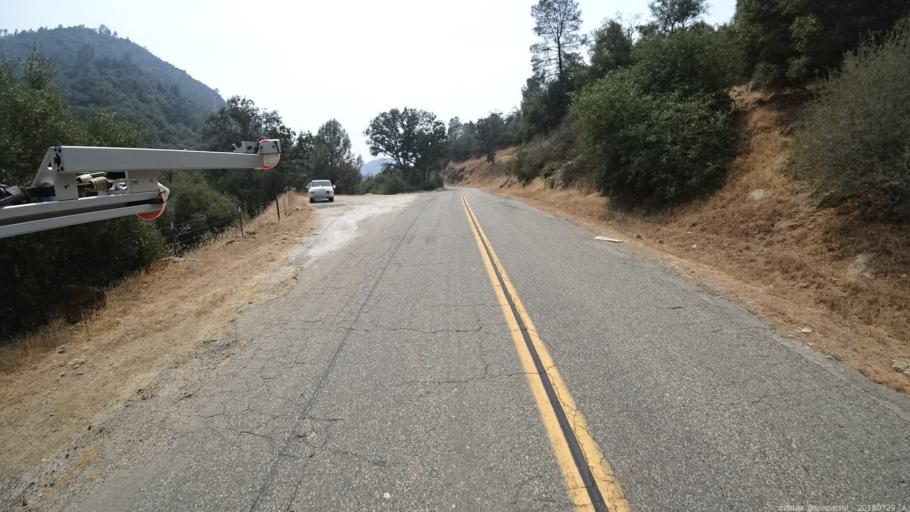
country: US
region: California
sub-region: Madera County
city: Ahwahnee
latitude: 37.3510
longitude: -119.7450
